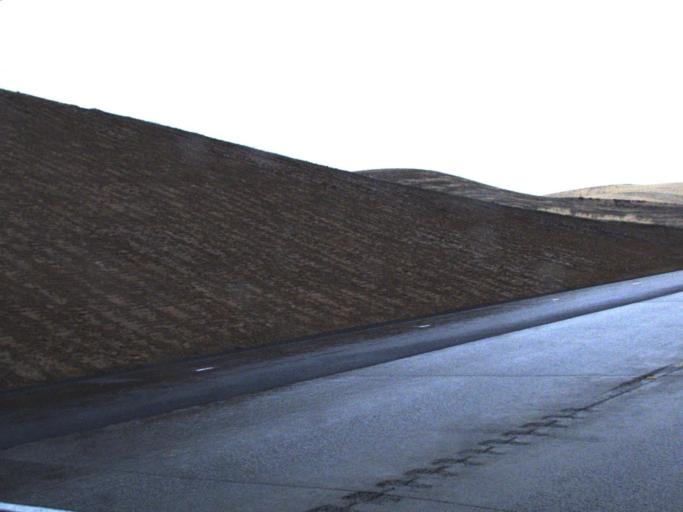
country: US
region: Washington
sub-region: Whitman County
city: Colfax
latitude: 46.9793
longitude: -117.3369
